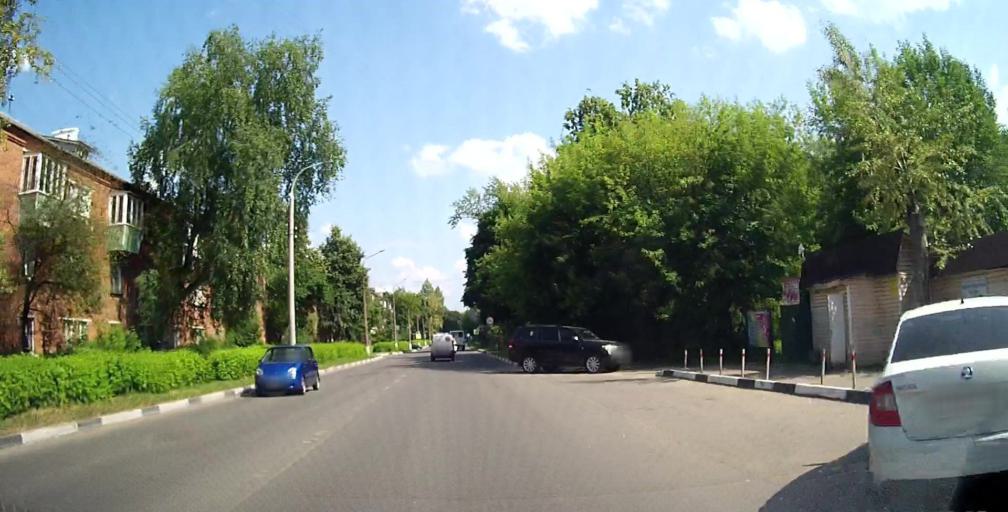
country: RU
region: Moskovskaya
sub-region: Podol'skiy Rayon
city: Podol'sk
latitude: 55.4148
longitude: 37.5329
